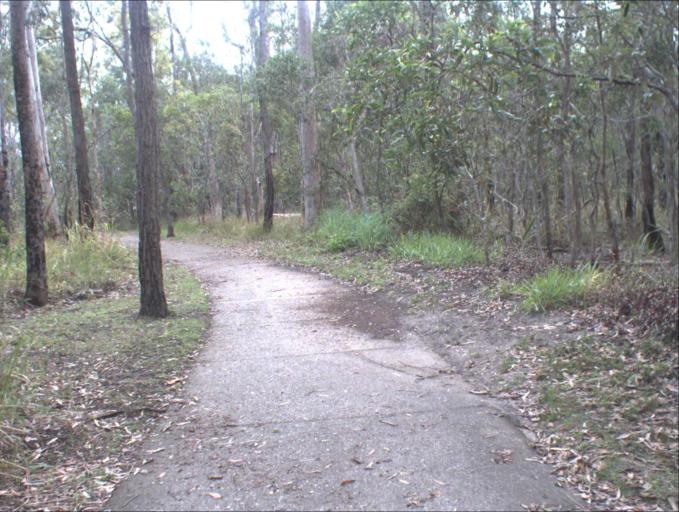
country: AU
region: Queensland
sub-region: Logan
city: Logan Reserve
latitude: -27.6876
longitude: 153.0669
